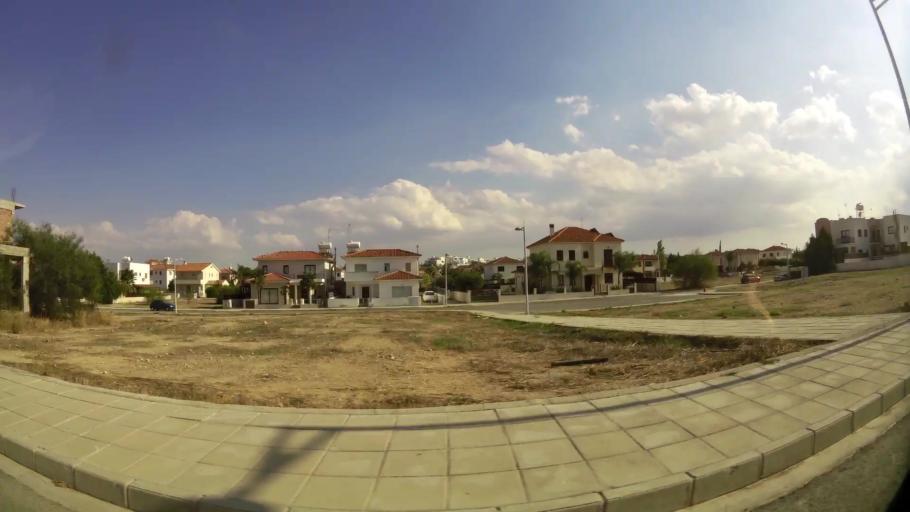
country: CY
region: Lefkosia
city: Nicosia
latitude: 35.1543
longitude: 33.2991
